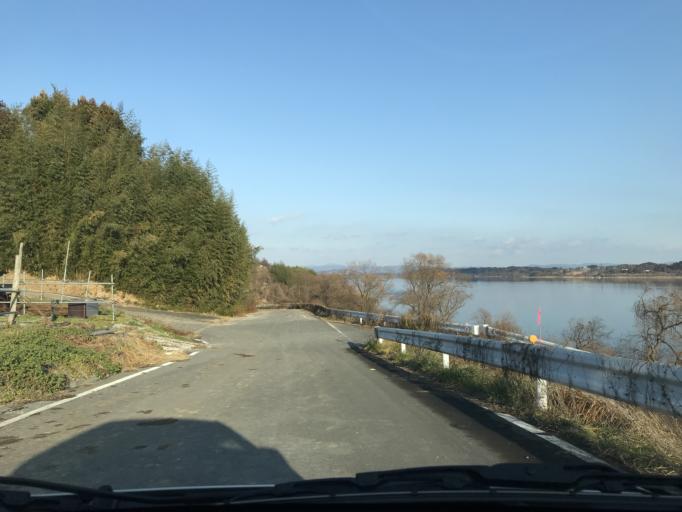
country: JP
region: Miyagi
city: Wakuya
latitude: 38.6972
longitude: 141.1264
